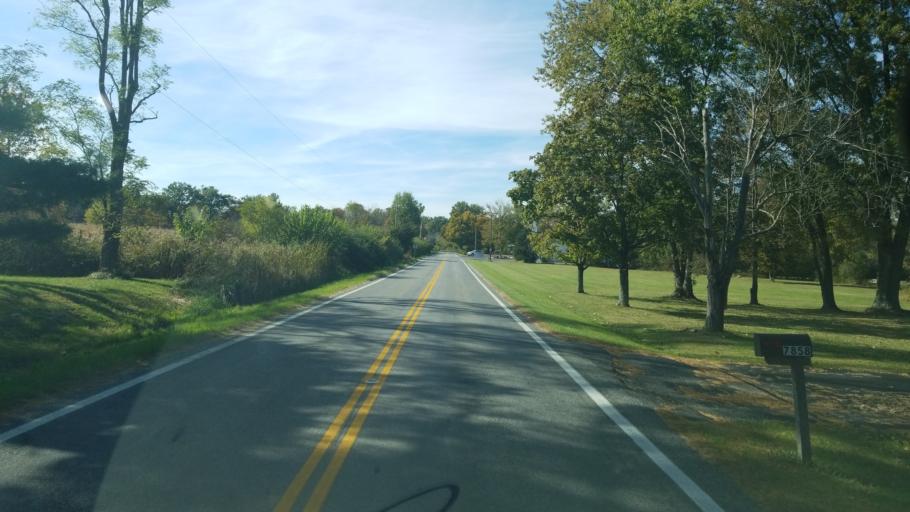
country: US
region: Ohio
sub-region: Warren County
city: Morrow
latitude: 39.4066
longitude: -84.0562
